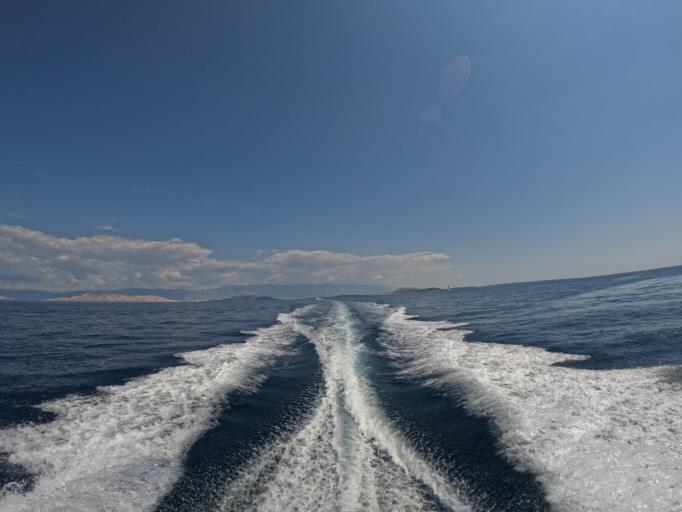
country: HR
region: Primorsko-Goranska
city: Punat
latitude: 44.8956
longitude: 14.6211
